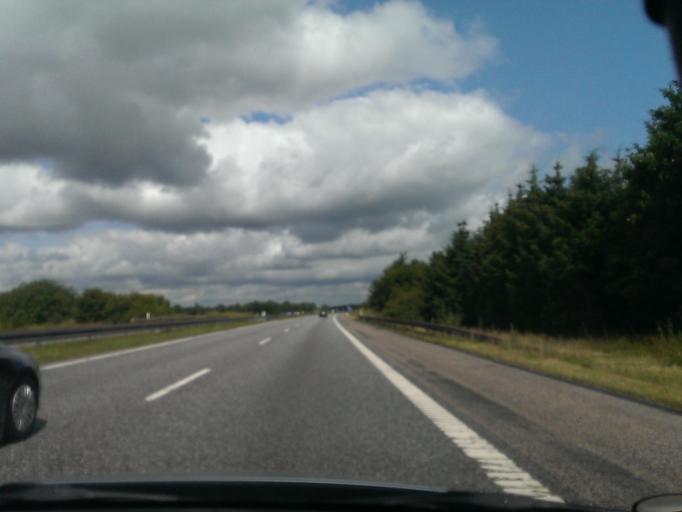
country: DK
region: North Denmark
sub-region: Mariagerfjord Kommune
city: Hobro
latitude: 56.5578
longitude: 9.8689
